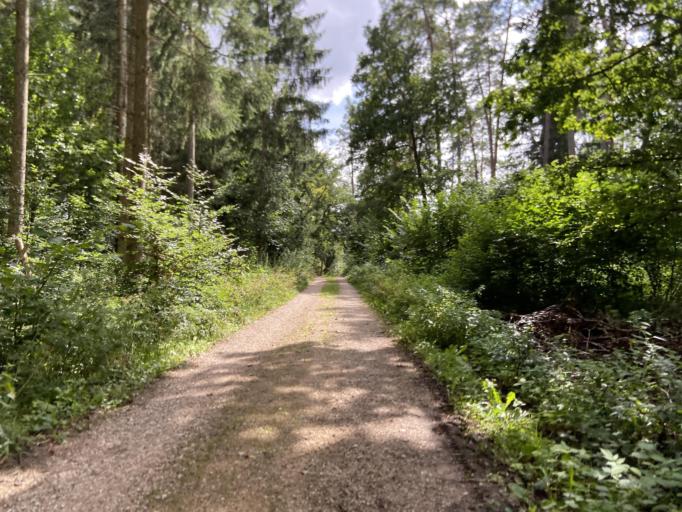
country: DE
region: Baden-Wuerttemberg
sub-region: Tuebingen Region
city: Bingen
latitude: 48.1249
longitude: 9.2804
